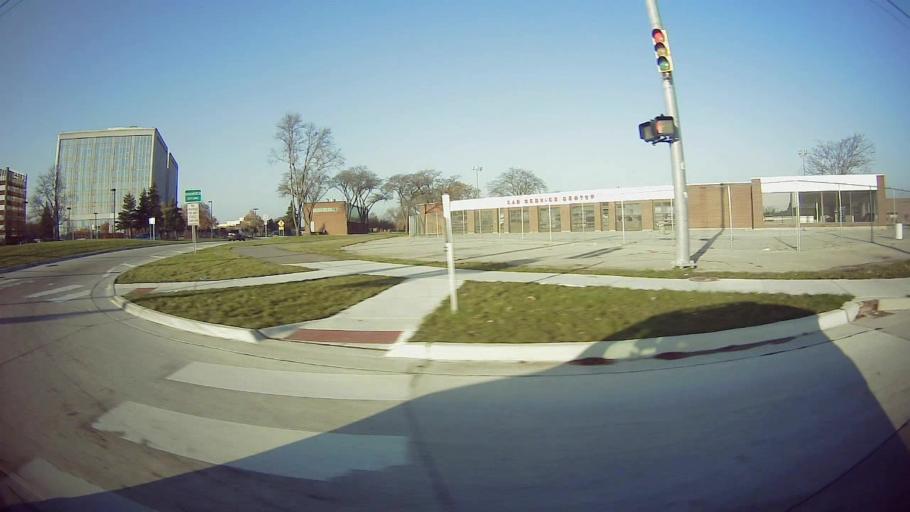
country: US
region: Michigan
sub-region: Oakland County
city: Oak Park
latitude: 42.4481
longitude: -83.2009
